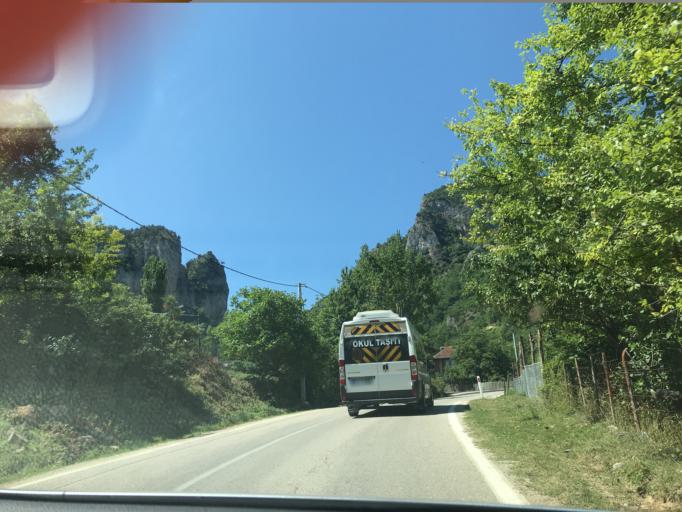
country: TR
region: Bursa
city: Tahtakopru
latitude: 39.9480
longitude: 29.5942
